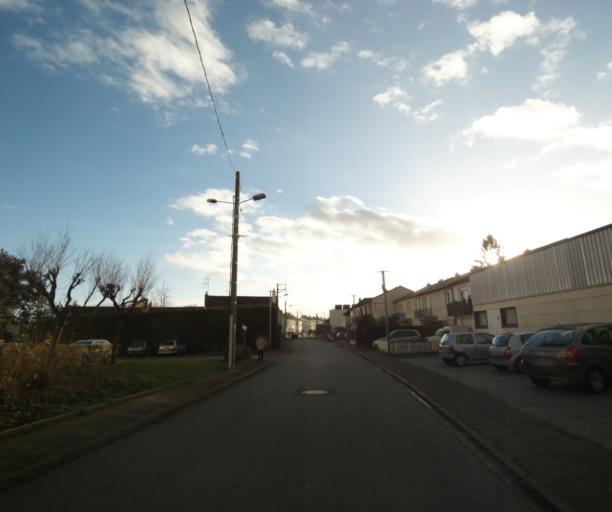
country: FR
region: Pays de la Loire
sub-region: Departement de la Sarthe
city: Le Mans
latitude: 47.9917
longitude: 0.1735
